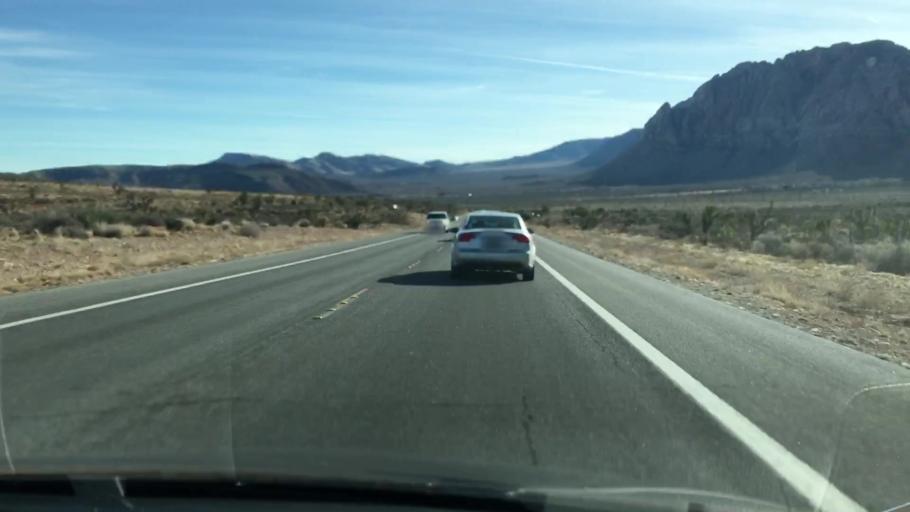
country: US
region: Nevada
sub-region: Clark County
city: Summerlin South
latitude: 36.0922
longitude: -115.4496
